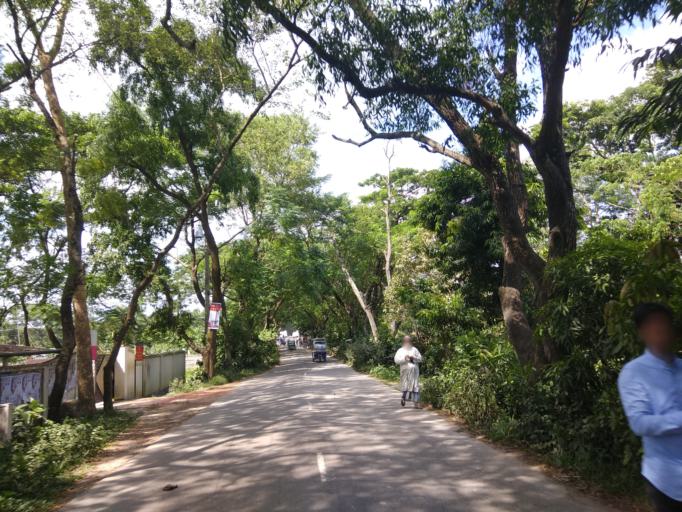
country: BD
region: Dhaka
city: Narayanganj
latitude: 23.5153
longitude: 90.4629
